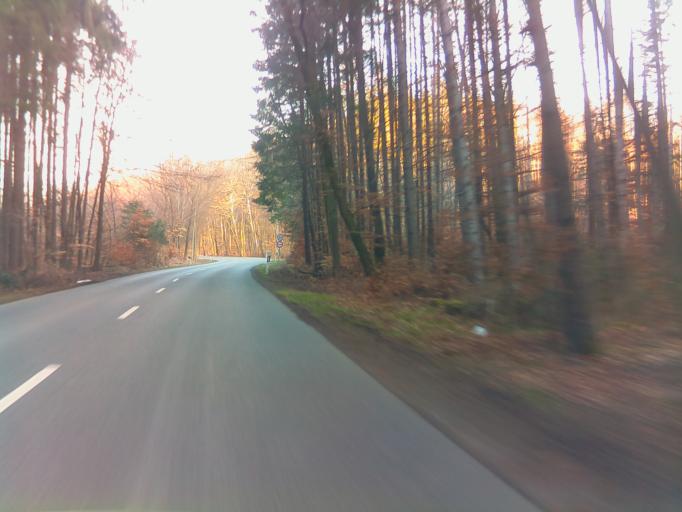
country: DE
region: Bavaria
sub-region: Upper Bavaria
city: Geltendorf
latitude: 48.1161
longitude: 11.0433
